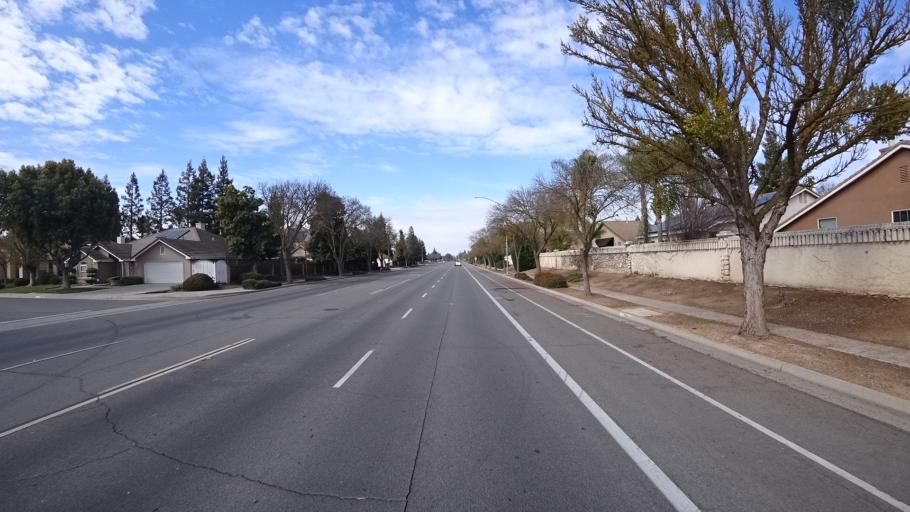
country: US
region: California
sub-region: Fresno County
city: West Park
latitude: 36.8442
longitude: -119.8820
